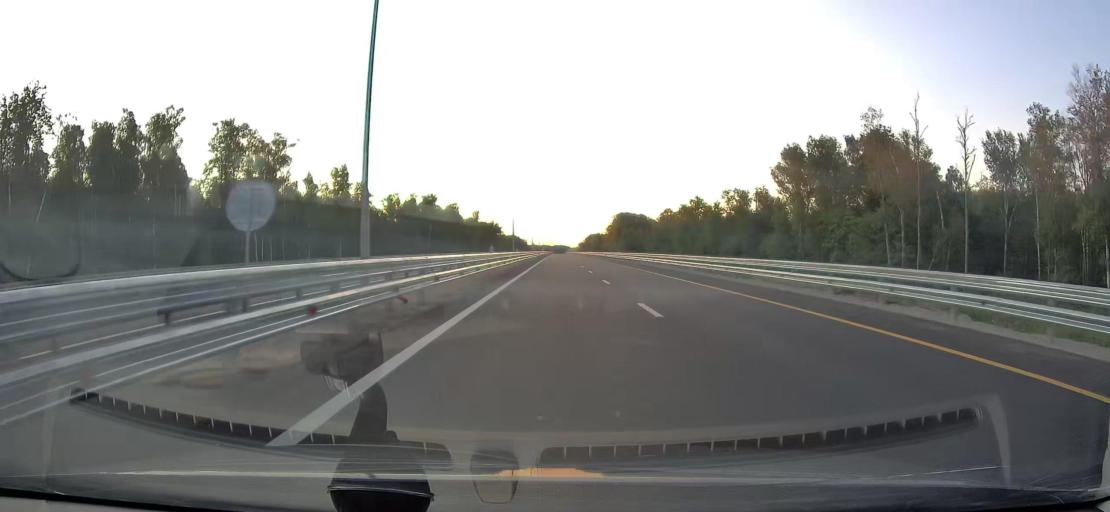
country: RU
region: Moskovskaya
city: L'vovskiy
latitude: 55.3418
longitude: 37.4848
